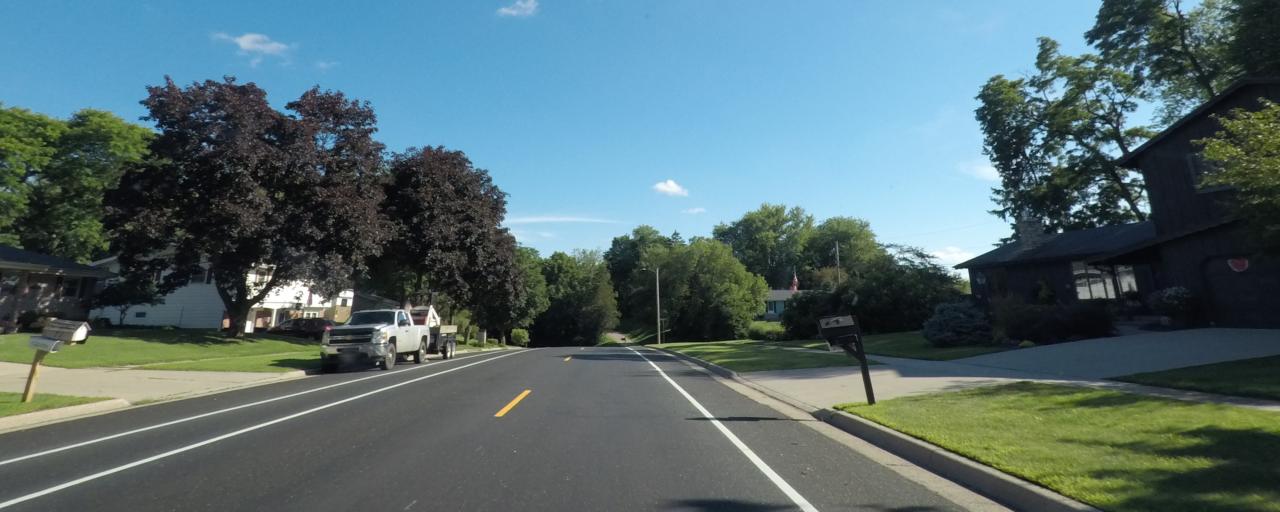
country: US
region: Wisconsin
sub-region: Rock County
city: Janesville
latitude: 42.6883
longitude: -88.9876
